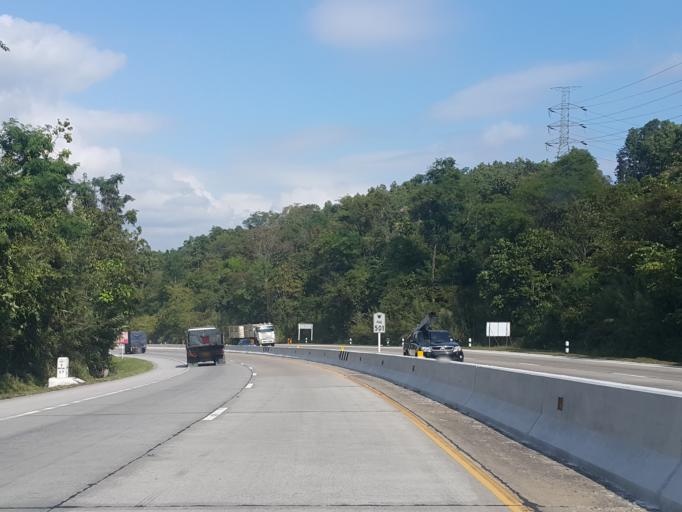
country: TH
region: Lamphun
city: Mae Tha
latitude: 18.4308
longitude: 99.2072
